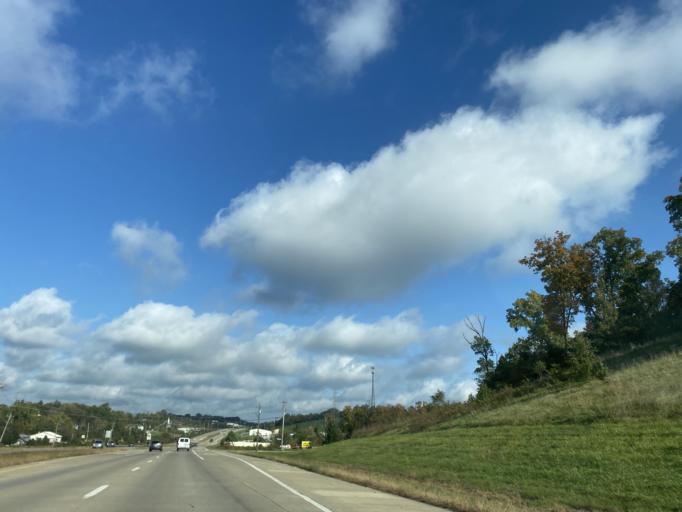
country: US
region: Kentucky
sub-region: Campbell County
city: Claryville
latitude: 38.9242
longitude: -84.3919
